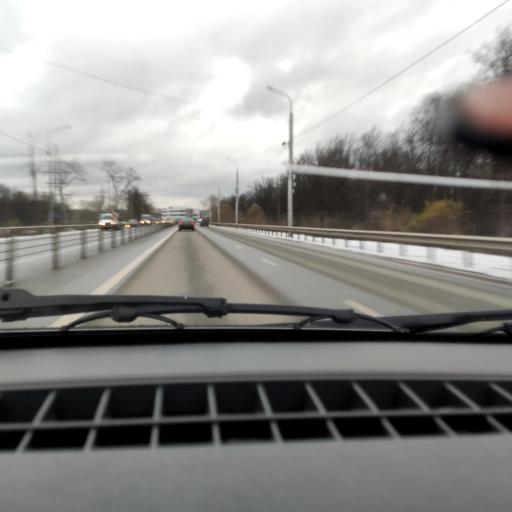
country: RU
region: Bashkortostan
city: Ufa
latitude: 54.6994
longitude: 55.8871
